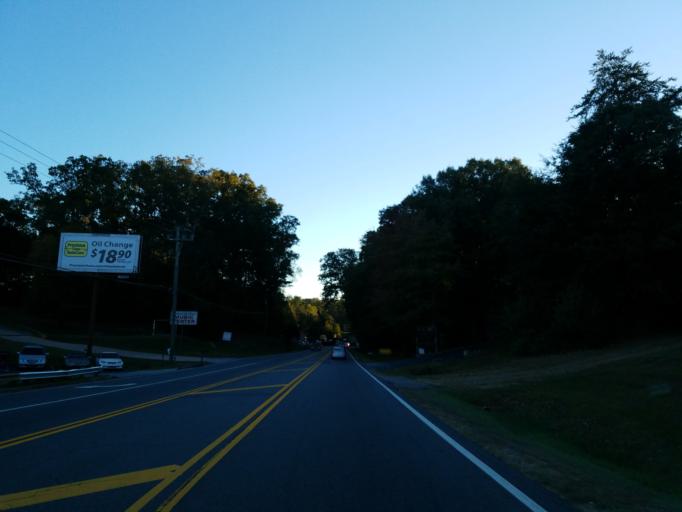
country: US
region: Georgia
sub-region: Forsyth County
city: Cumming
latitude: 34.2317
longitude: -84.1248
